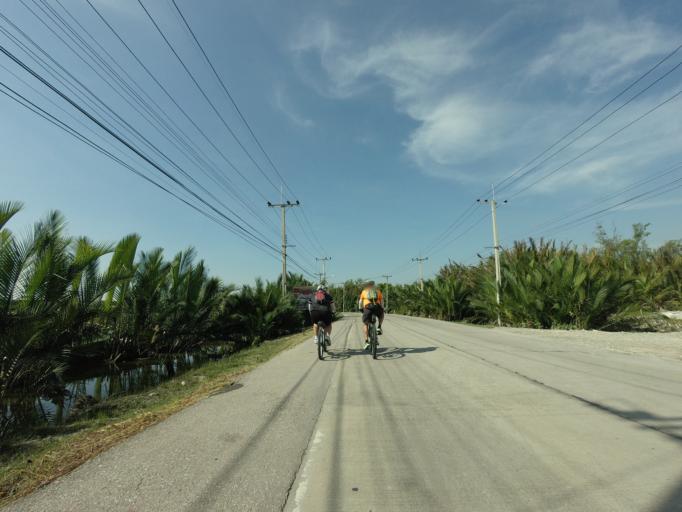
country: TH
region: Samut Prakan
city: Phra Samut Chedi
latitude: 13.5628
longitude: 100.5440
